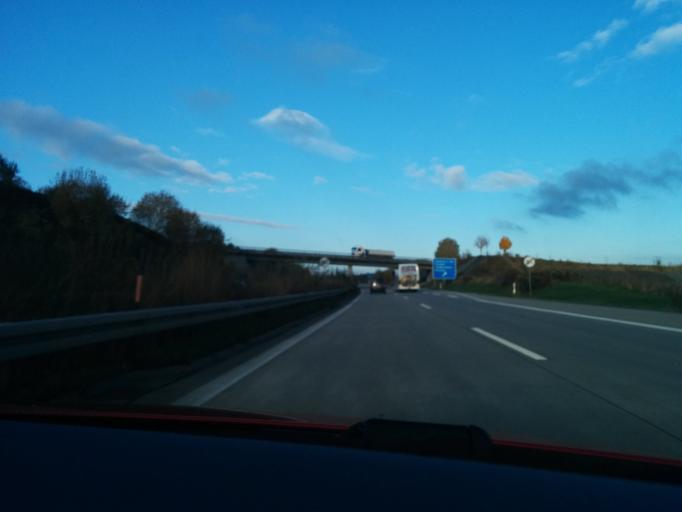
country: DE
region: Saxony
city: Dohna
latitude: 50.9752
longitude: 13.8114
